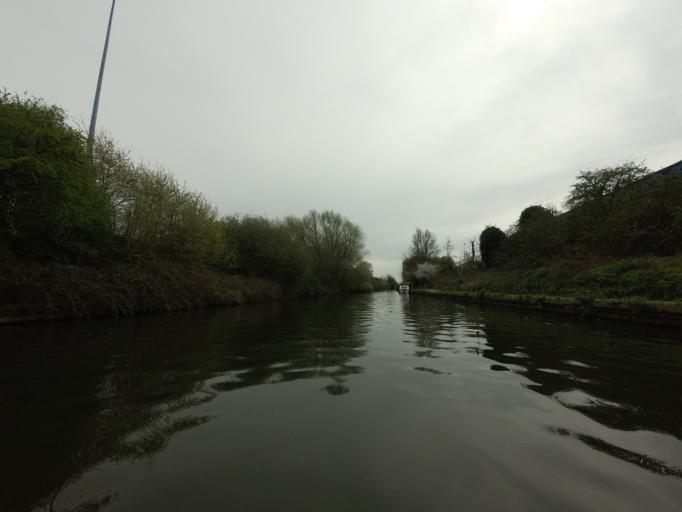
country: GB
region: England
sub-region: Greater London
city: Acton
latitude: 51.5323
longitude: -0.2538
